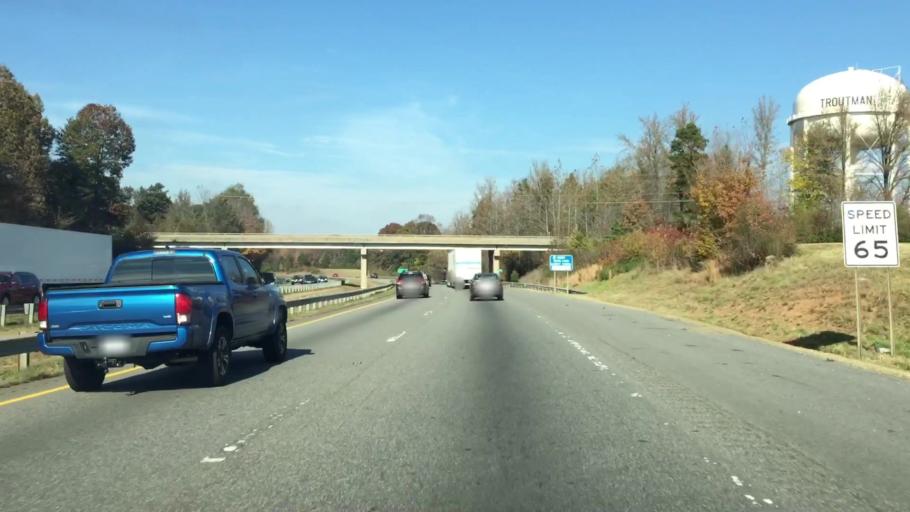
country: US
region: North Carolina
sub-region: Iredell County
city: Troutman
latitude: 35.6796
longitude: -80.8535
